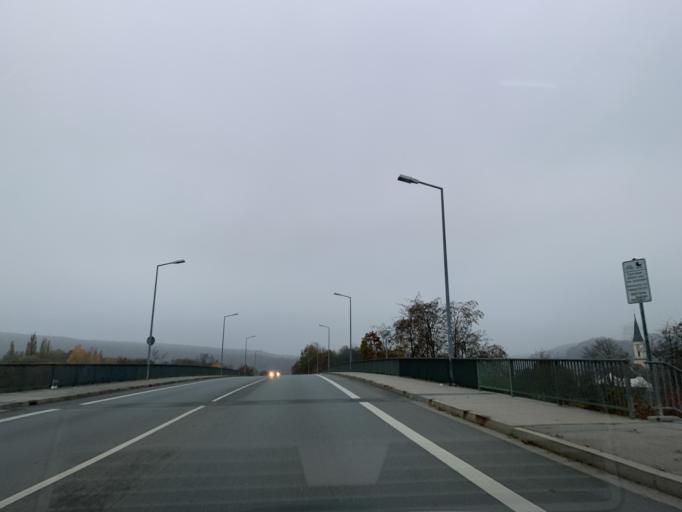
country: DE
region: Bavaria
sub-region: Lower Bavaria
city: Kelheim
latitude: 48.9185
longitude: 11.8797
